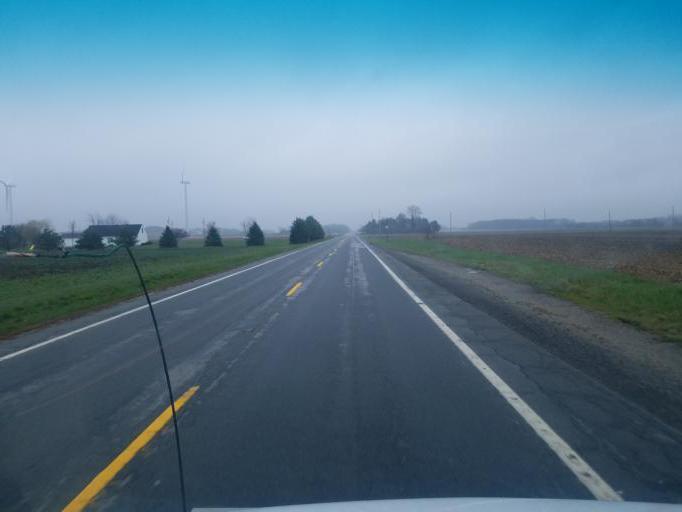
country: US
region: Ohio
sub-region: Wood County
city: Weston
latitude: 41.3722
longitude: -83.7499
